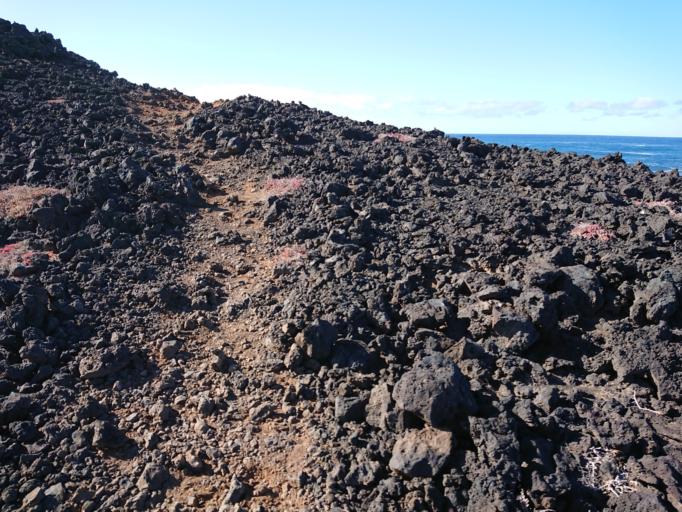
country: ES
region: Canary Islands
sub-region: Provincia de Las Palmas
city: Tinajo
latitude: 29.0811
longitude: -13.7286
